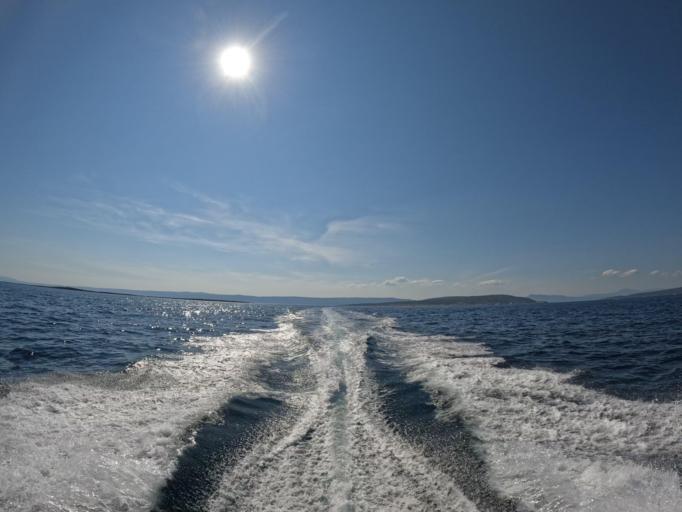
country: HR
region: Primorsko-Goranska
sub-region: Grad Krk
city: Krk
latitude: 44.9541
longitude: 14.5867
